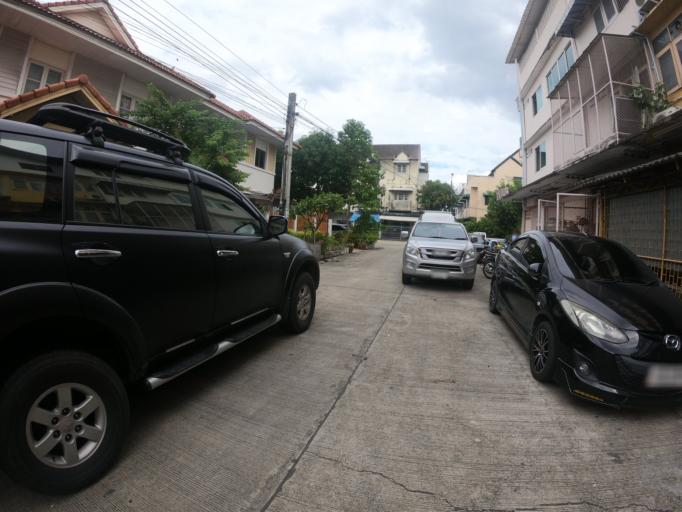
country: TH
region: Bangkok
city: Suan Luang
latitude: 13.7100
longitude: 100.6635
